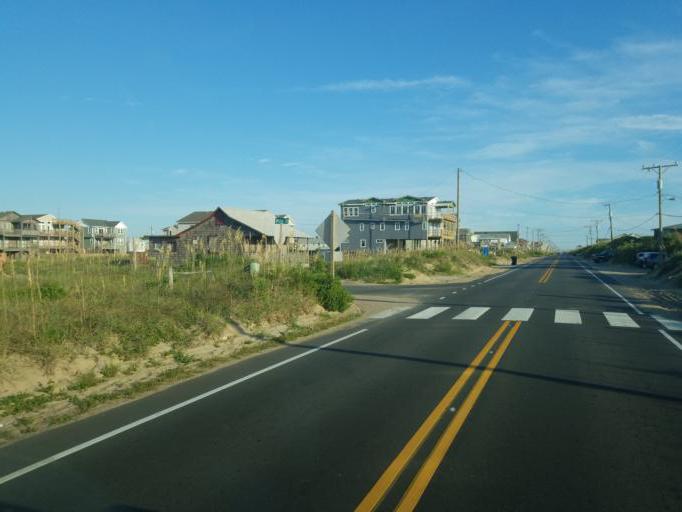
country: US
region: North Carolina
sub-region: Dare County
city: Kitty Hawk
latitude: 36.0610
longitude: -75.6865
